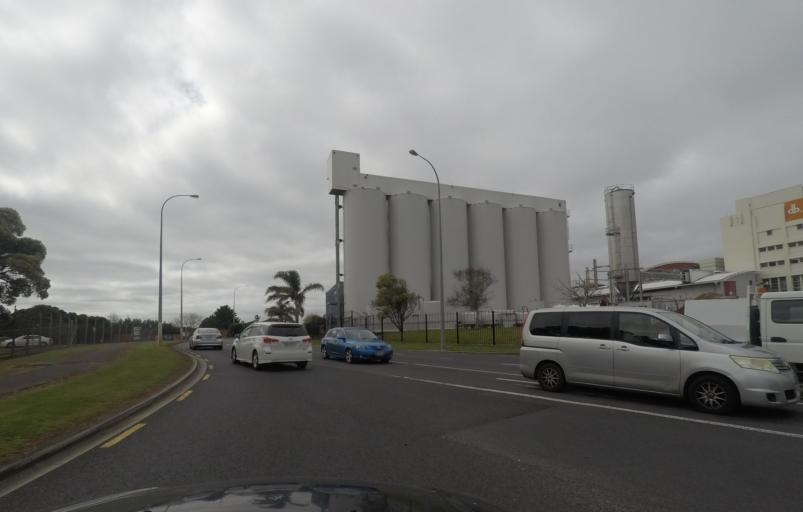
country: NZ
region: Auckland
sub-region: Auckland
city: Wiri
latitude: -36.9573
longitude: 174.8529
